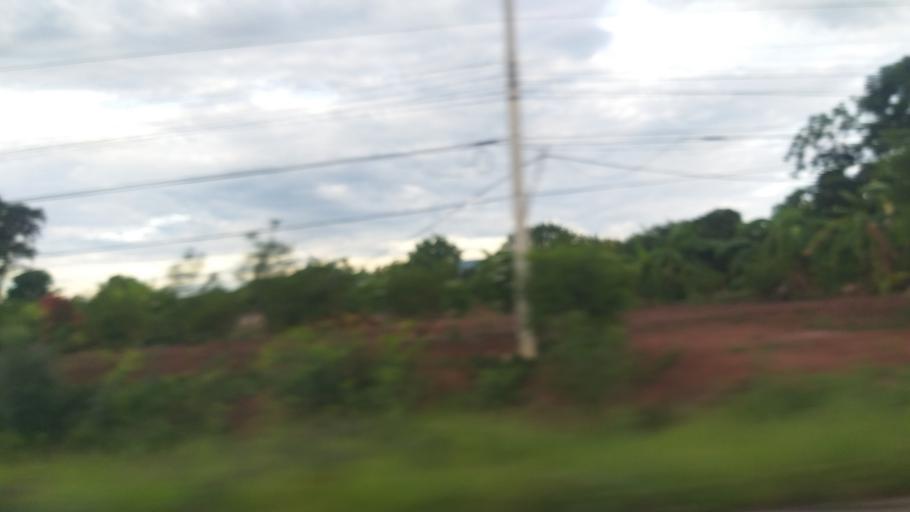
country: TH
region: Chaiyaphum
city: Kaeng Khro
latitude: 16.1855
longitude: 102.2119
